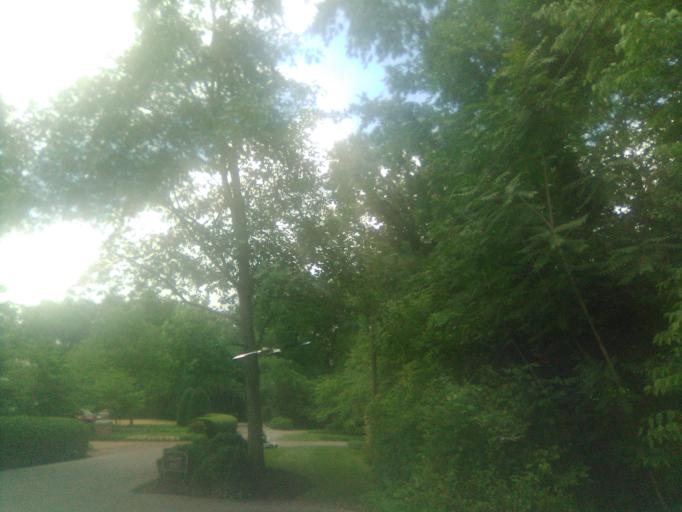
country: US
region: Tennessee
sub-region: Davidson County
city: Belle Meade
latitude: 36.1085
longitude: -86.8463
